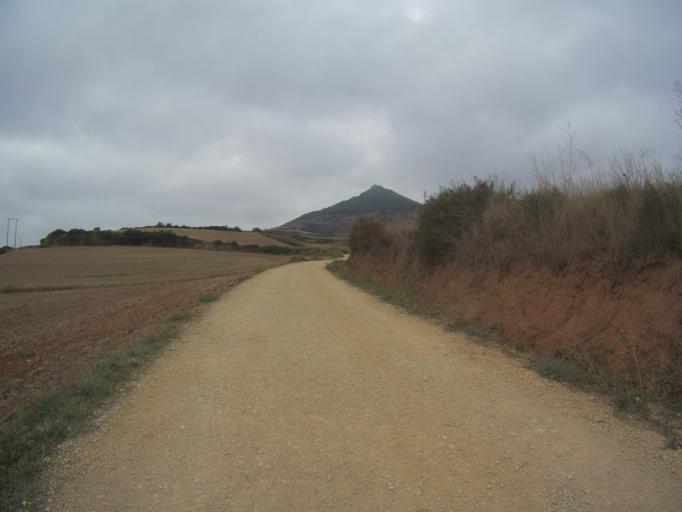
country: ES
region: Navarre
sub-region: Provincia de Navarra
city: Iguzquiza
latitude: 42.6332
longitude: -2.0906
